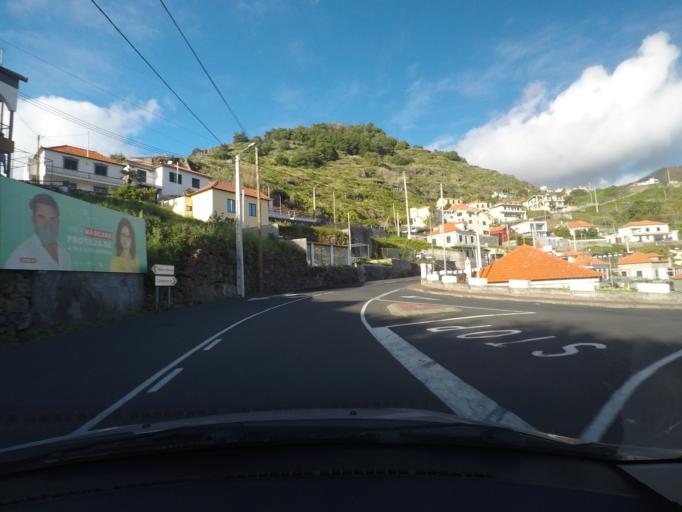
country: PT
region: Madeira
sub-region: Ribeira Brava
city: Campanario
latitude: 32.6680
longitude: -17.0363
